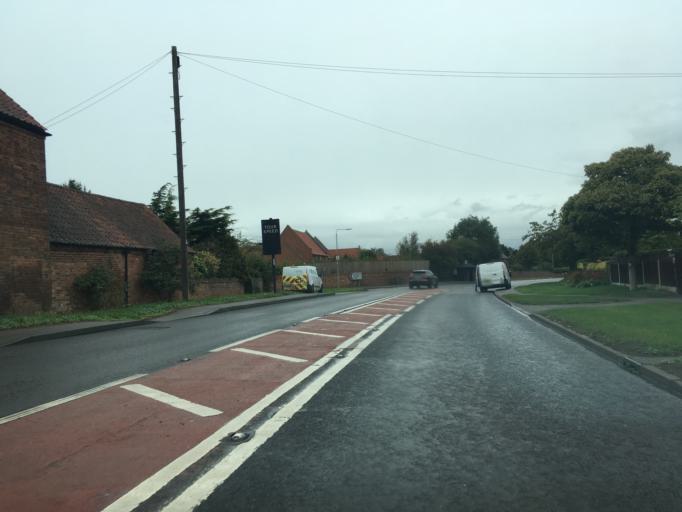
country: GB
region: England
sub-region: Nottinghamshire
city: Ruddington
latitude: 52.8748
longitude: -1.1312
